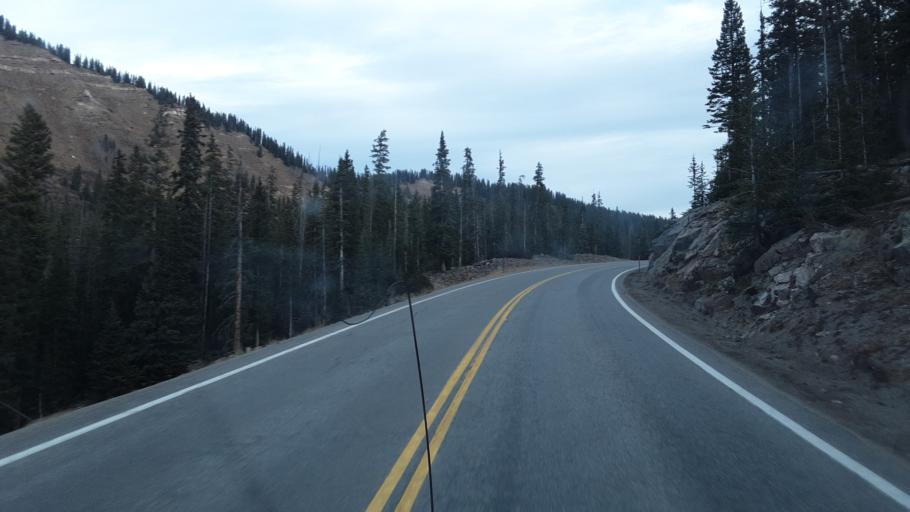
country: US
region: Colorado
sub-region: San Juan County
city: Silverton
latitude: 37.6914
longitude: -107.7793
